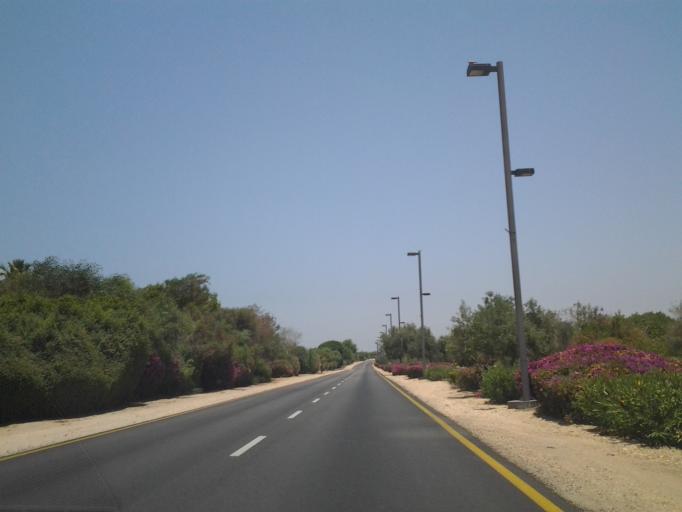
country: IL
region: Haifa
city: Qesarya
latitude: 32.5160
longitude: 34.9064
